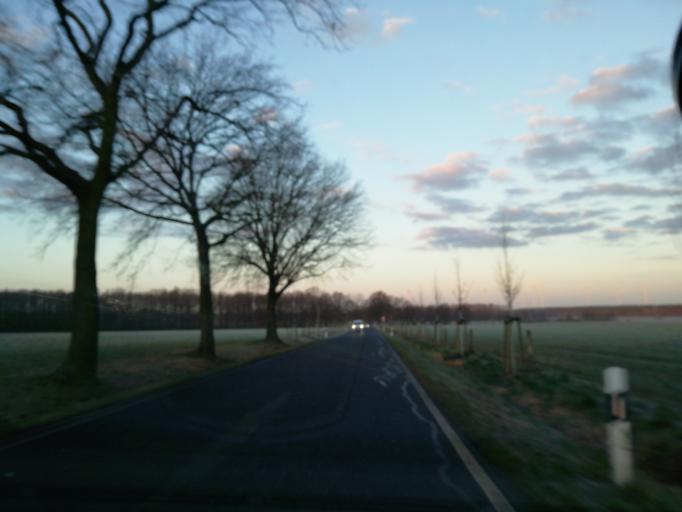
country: DE
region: Brandenburg
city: Calau
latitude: 51.7384
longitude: 13.9266
